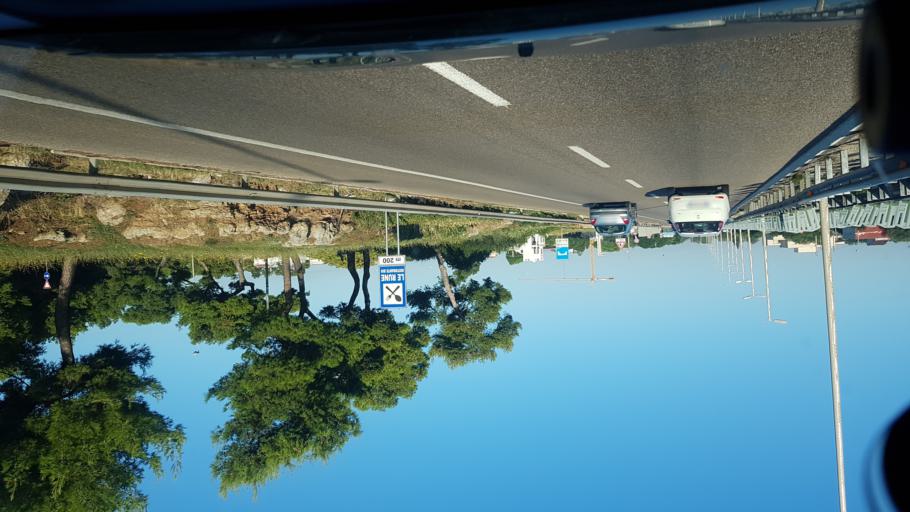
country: IT
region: Apulia
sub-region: Provincia di Bari
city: Parco Scizzo-Parchitello
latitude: 41.0831
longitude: 17.0013
